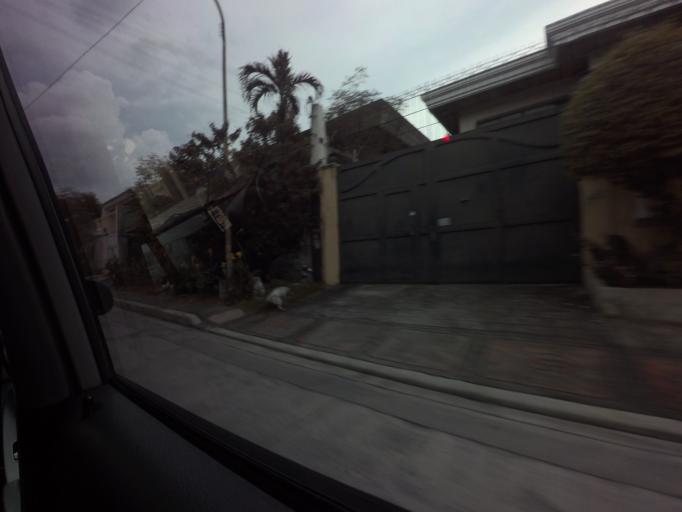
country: PH
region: Calabarzon
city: Del Monte
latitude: 14.6172
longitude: 121.0062
